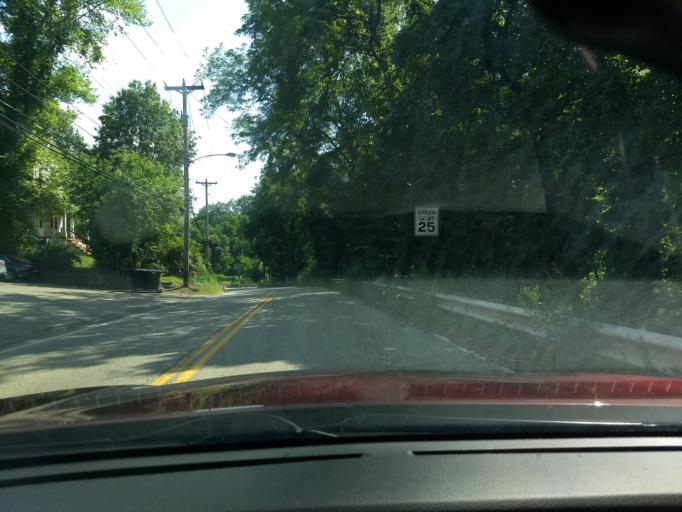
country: US
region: Pennsylvania
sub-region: Allegheny County
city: West Homestead
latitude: 40.3865
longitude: -79.9126
